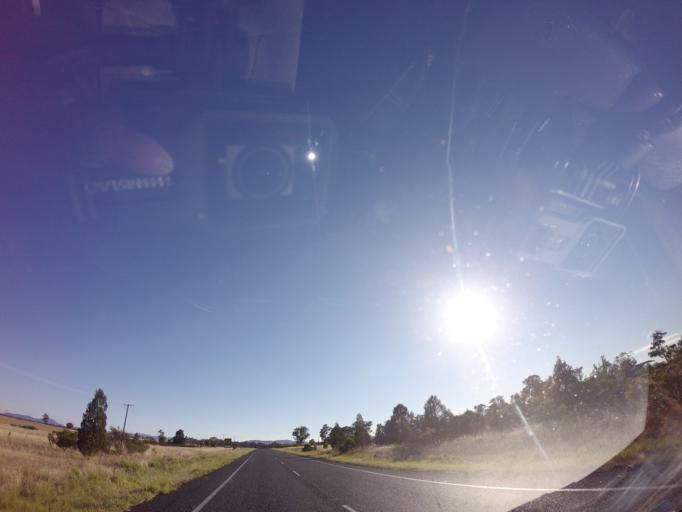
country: AU
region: New South Wales
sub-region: Gilgandra
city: Gilgandra
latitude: -31.5627
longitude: 148.7968
